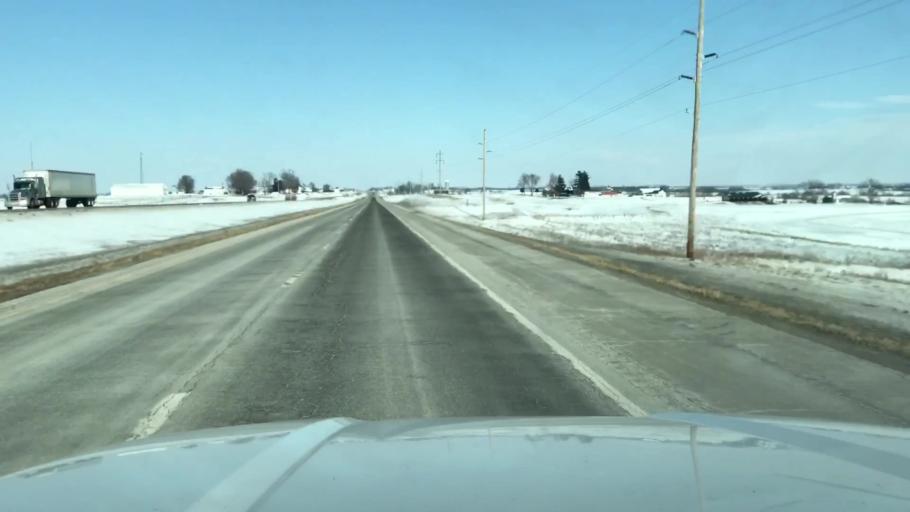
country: US
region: Missouri
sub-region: Nodaway County
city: Maryville
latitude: 40.2335
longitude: -94.8675
